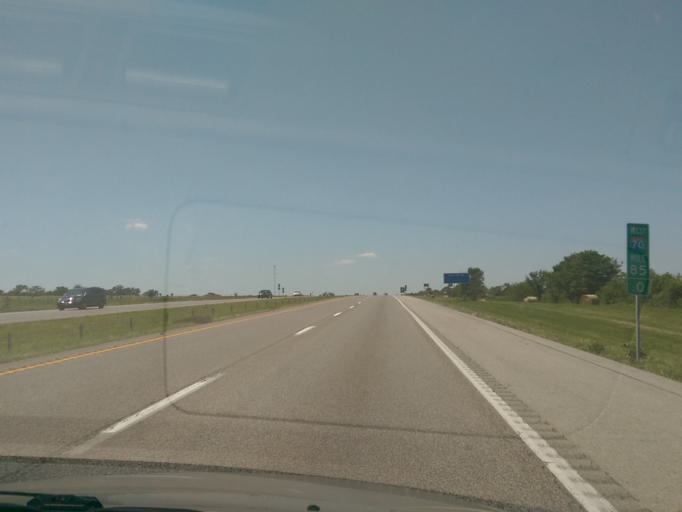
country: US
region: Missouri
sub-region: Saline County
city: Marshall
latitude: 38.9526
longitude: -93.0795
